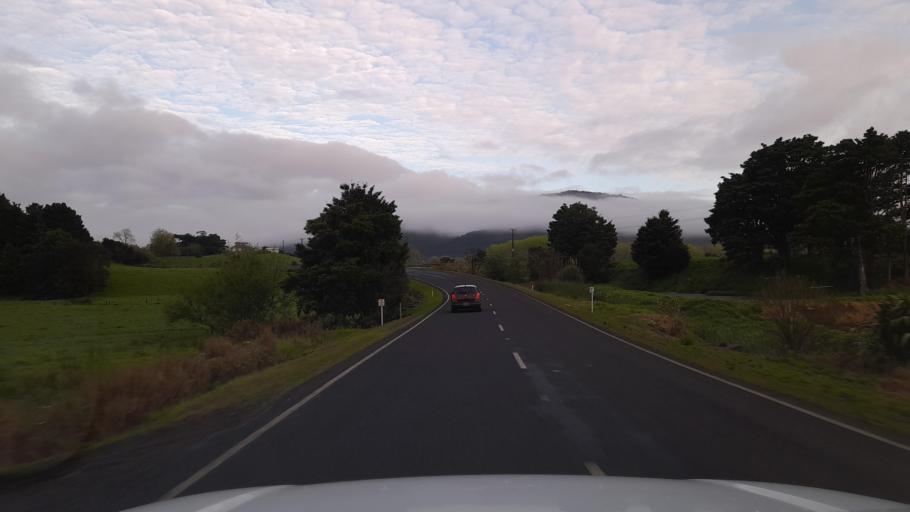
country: NZ
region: Northland
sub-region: Whangarei
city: Maungatapere
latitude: -35.7081
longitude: 173.9865
